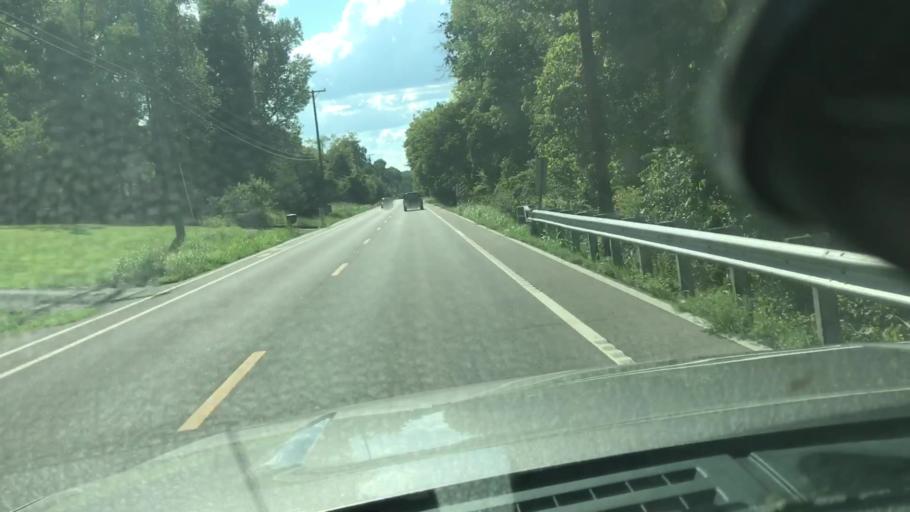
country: US
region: Tennessee
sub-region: Cheatham County
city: Pegram
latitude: 36.0290
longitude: -87.0030
